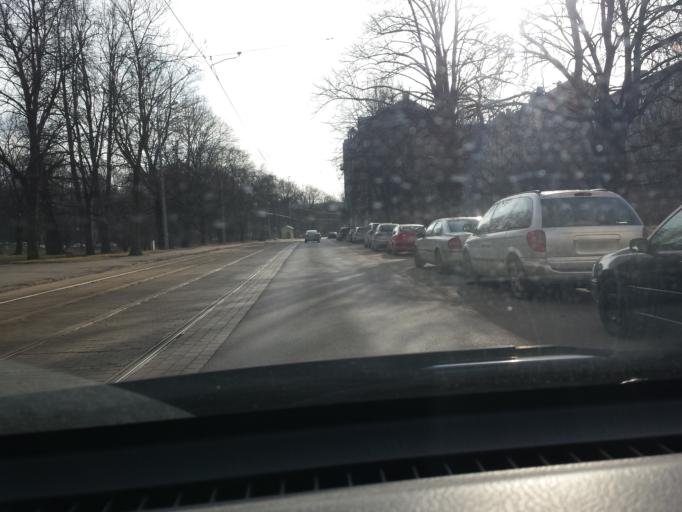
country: LV
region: Riga
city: Riga
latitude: 56.9743
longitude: 24.1429
